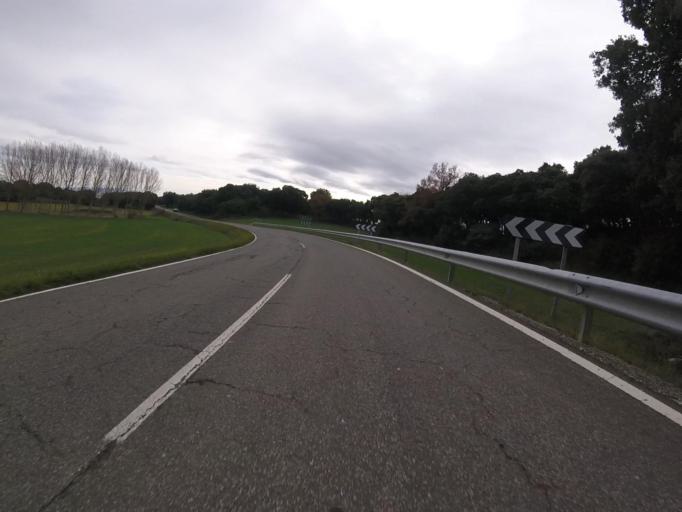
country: ES
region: Navarre
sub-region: Provincia de Navarra
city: Lezaun
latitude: 42.7525
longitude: -2.0178
